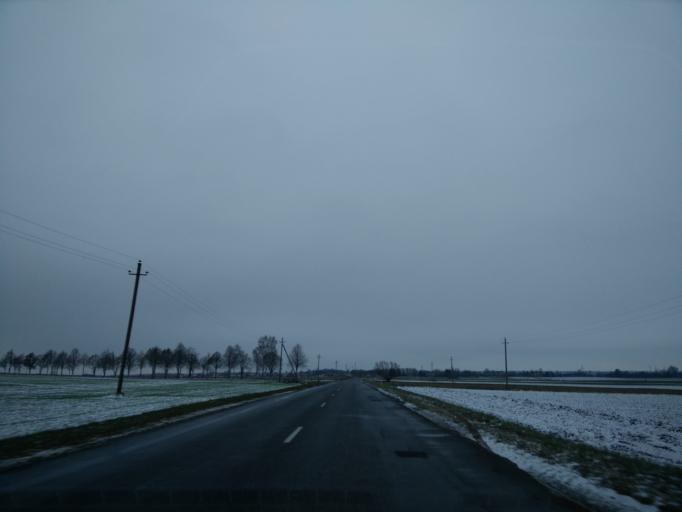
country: LT
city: Ariogala
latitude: 55.3513
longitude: 23.3837
